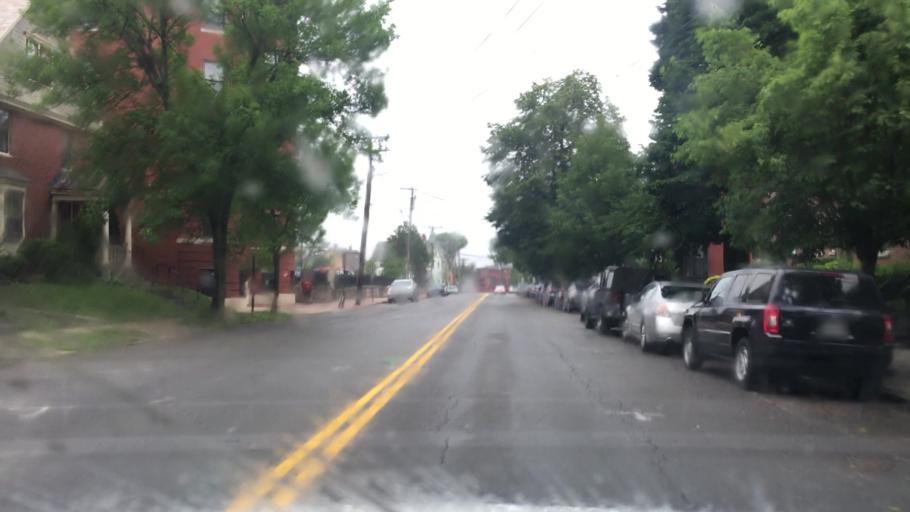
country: US
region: Maine
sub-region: Cumberland County
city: Portland
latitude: 43.6512
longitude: -70.2732
